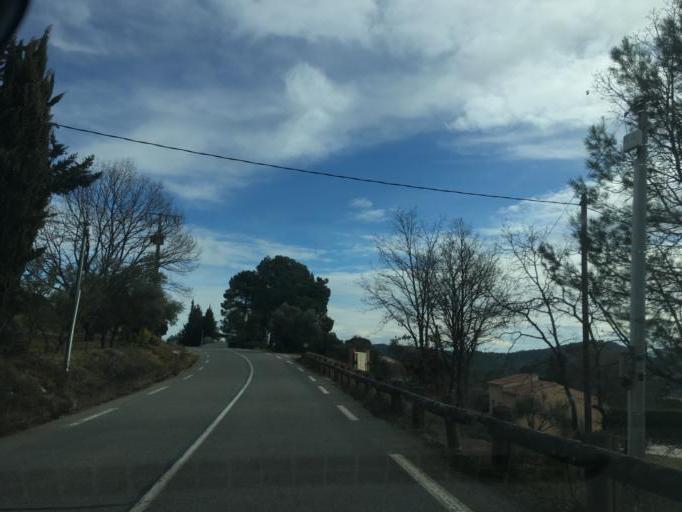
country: FR
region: Provence-Alpes-Cote d'Azur
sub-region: Departement du Var
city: Le Val
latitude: 43.4411
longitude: 6.0461
